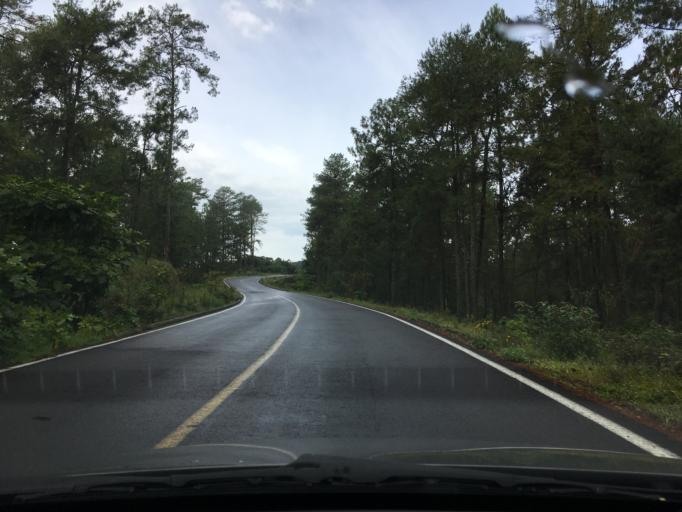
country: MX
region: Michoacan
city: Nuevo San Juan Parangaricutiro
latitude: 19.4435
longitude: -102.1606
